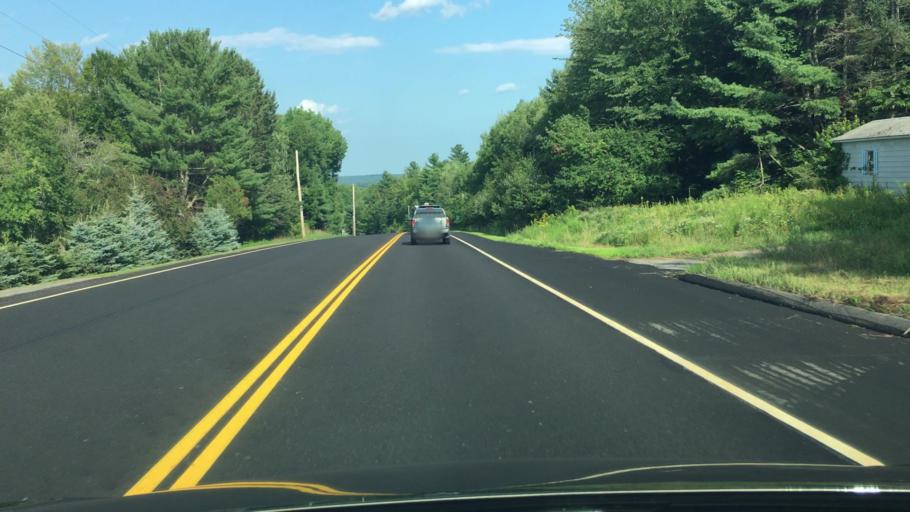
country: US
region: Maine
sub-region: Waldo County
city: Searsmont
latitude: 44.4002
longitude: -69.2498
